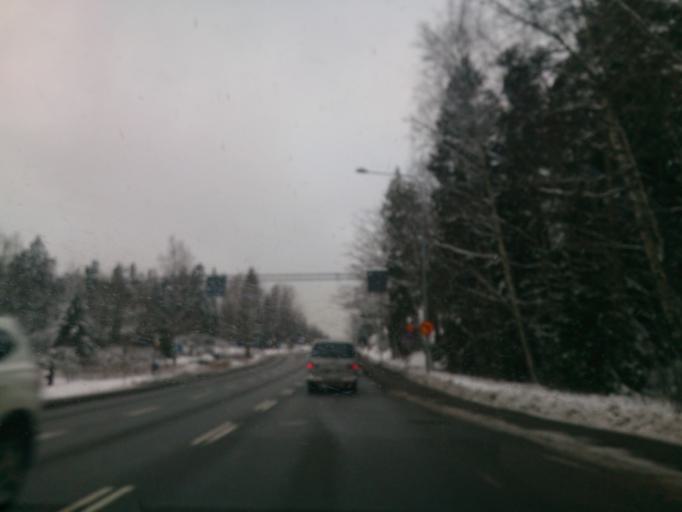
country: SE
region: Stockholm
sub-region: Varmdo Kommun
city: Mortnas
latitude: 59.3134
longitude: 18.4402
